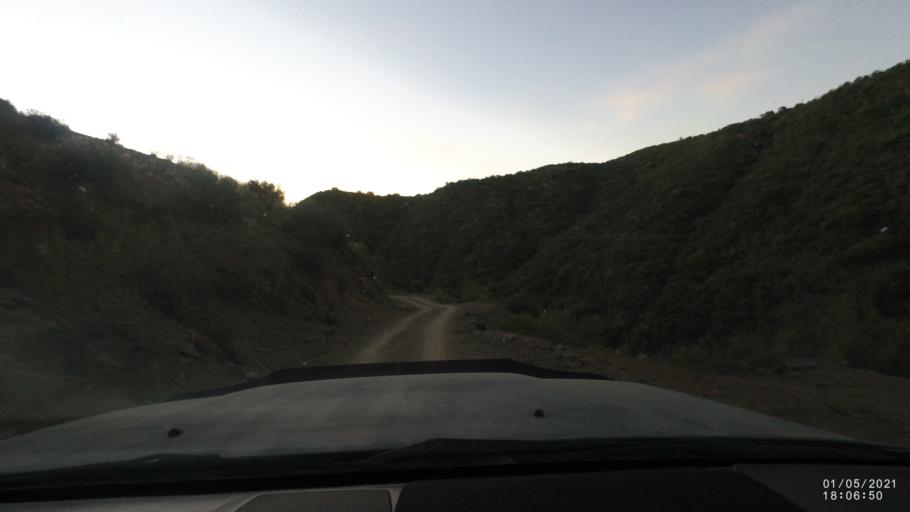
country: BO
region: Cochabamba
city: Capinota
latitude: -17.6854
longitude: -66.1870
